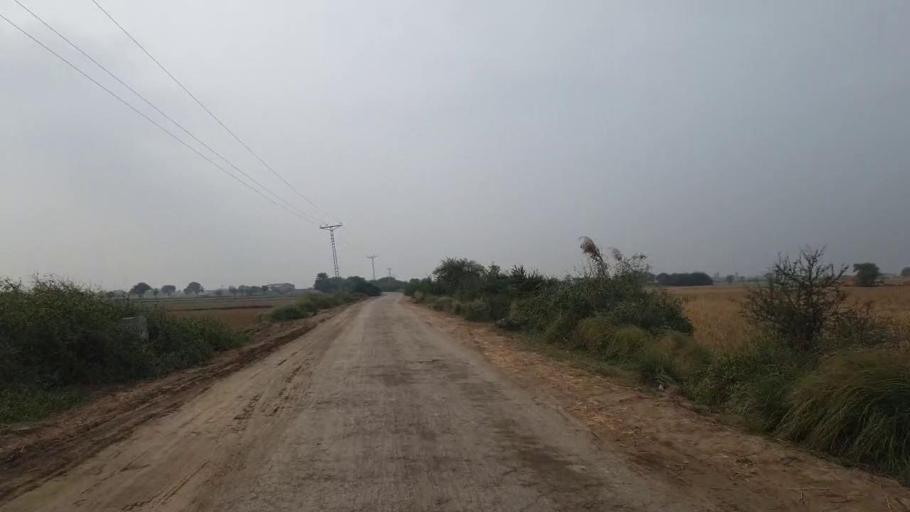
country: PK
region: Sindh
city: Matli
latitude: 24.9456
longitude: 68.5773
